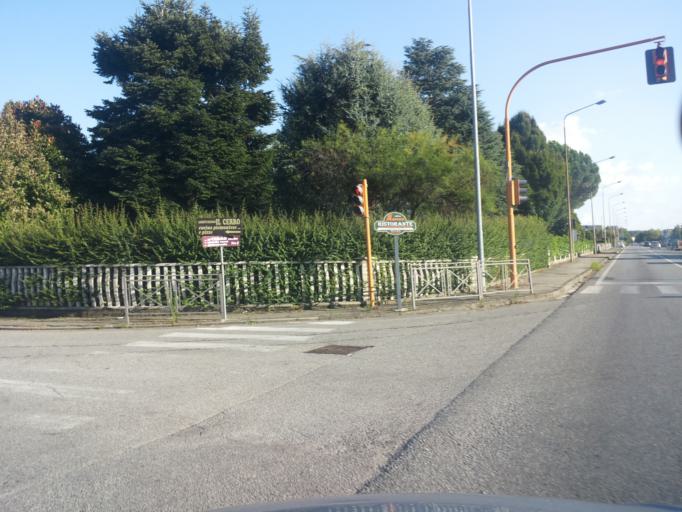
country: IT
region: Piedmont
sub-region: Provincia di Torino
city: Romano Canavese
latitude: 45.3966
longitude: 7.8841
